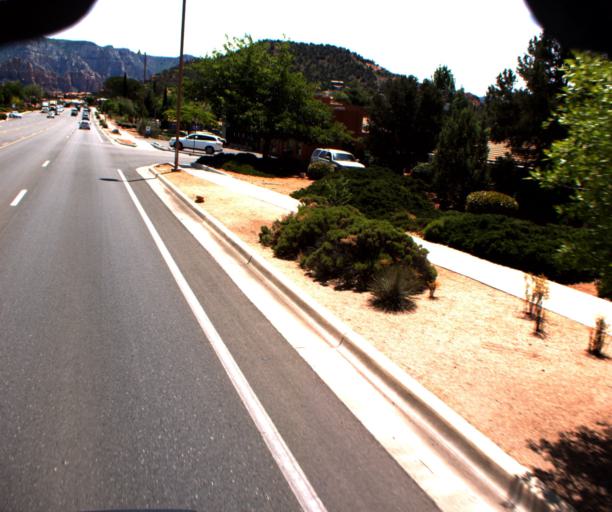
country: US
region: Arizona
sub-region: Yavapai County
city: West Sedona
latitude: 34.8630
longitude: -111.7865
